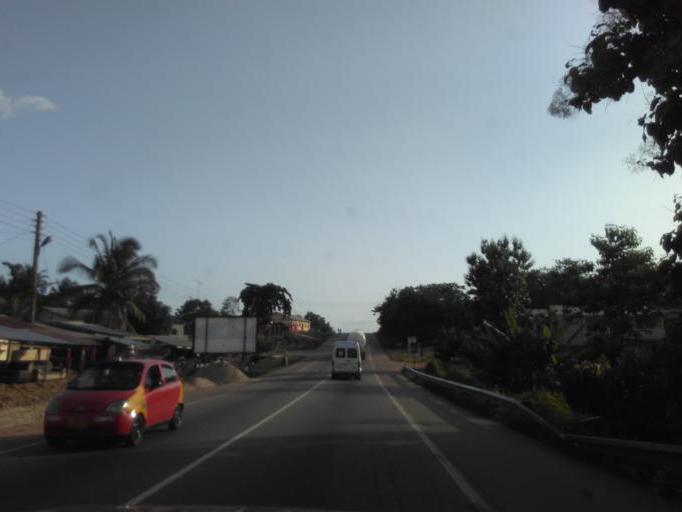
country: GH
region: Ashanti
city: Konongo
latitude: 6.6182
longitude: -1.2320
